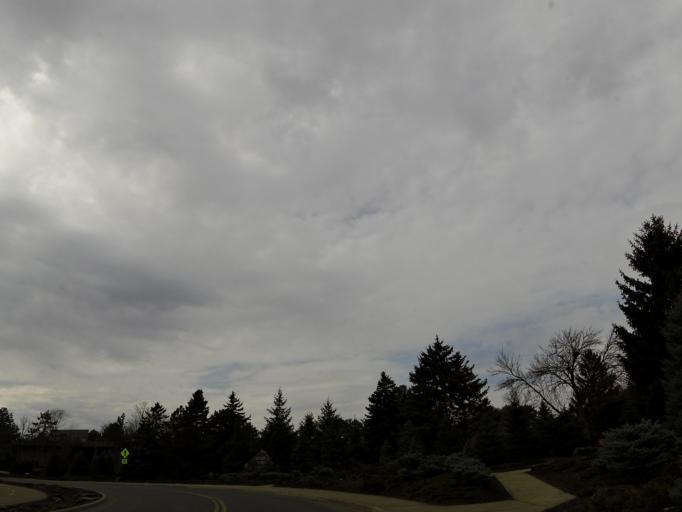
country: US
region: Minnesota
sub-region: Hennepin County
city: Edina
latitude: 44.8709
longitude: -93.3312
